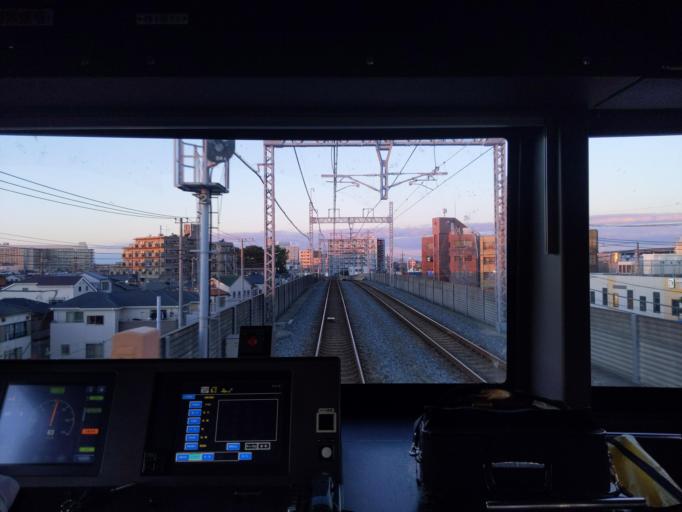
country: JP
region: Chiba
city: Shiroi
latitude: 35.7711
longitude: 139.9990
